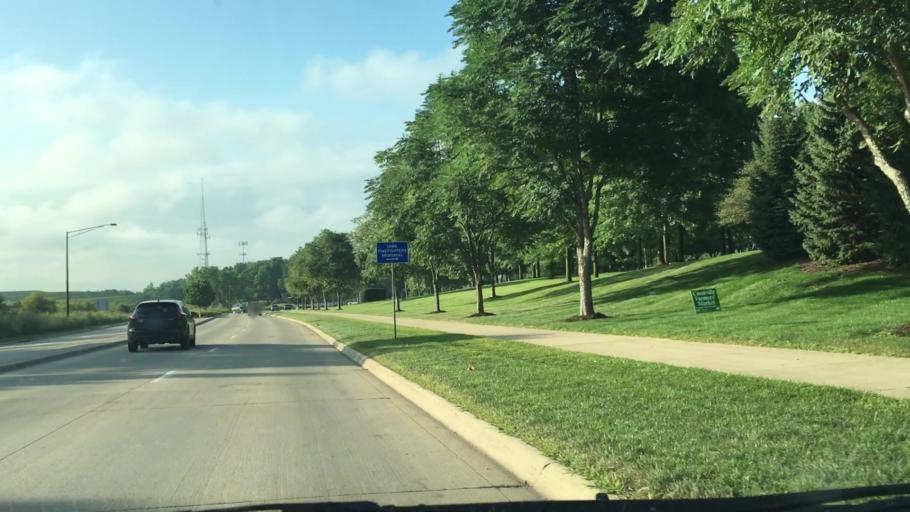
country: US
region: Iowa
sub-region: Johnson County
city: Coralville
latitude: 41.6916
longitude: -91.5661
